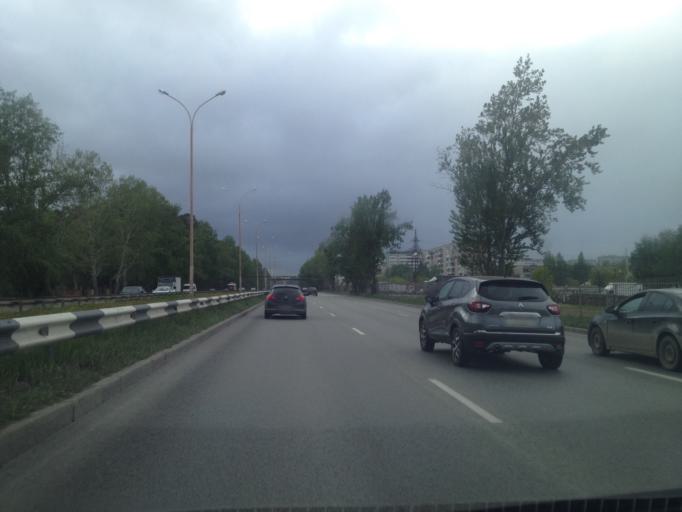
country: RU
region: Sverdlovsk
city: Sovkhoznyy
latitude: 56.7963
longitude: 60.5610
